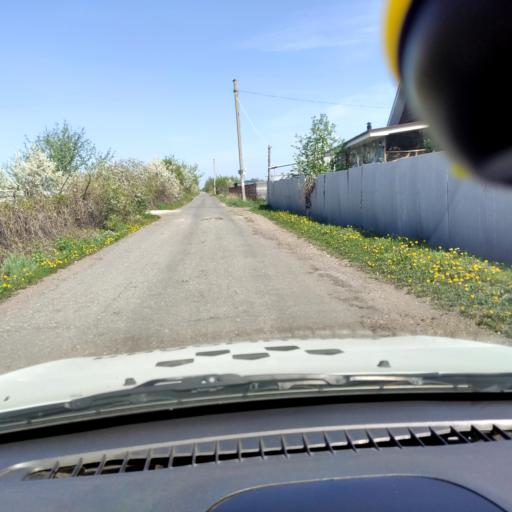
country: RU
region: Samara
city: Tol'yatti
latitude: 53.6673
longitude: 49.3630
